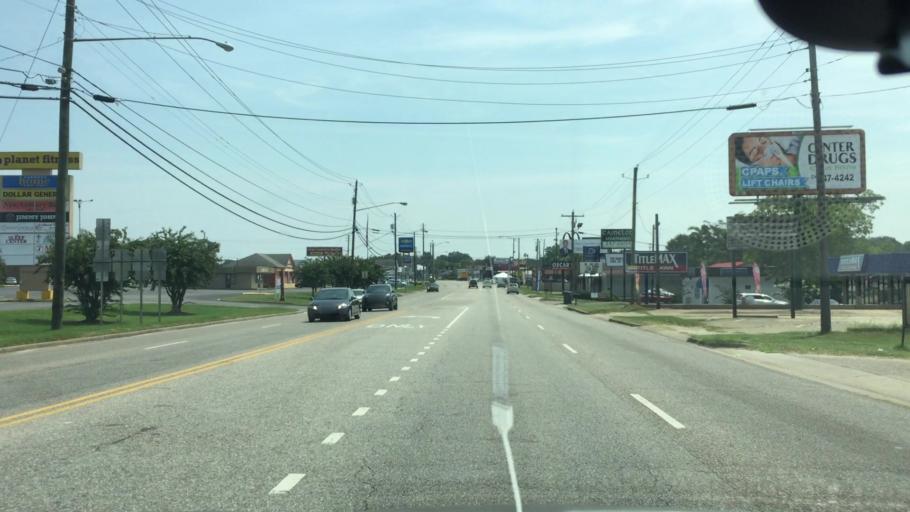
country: US
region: Alabama
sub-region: Coffee County
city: Enterprise
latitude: 31.3236
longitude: -85.8284
